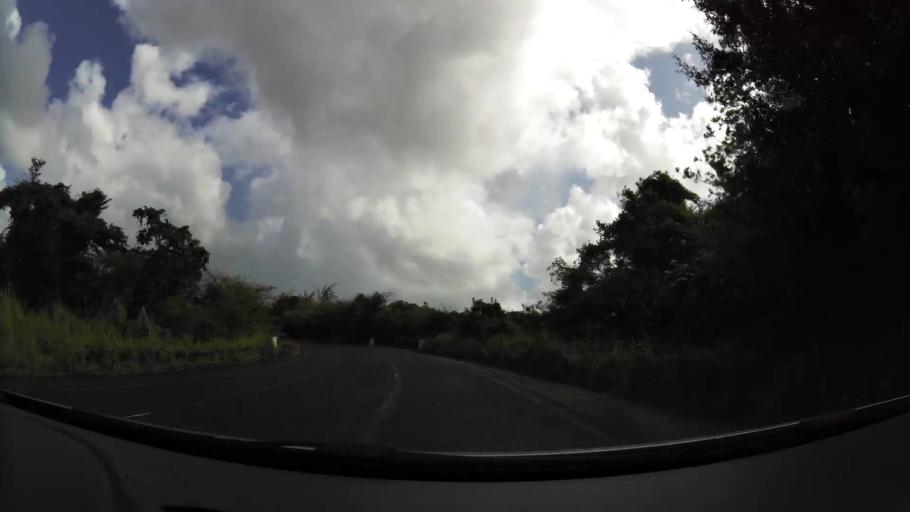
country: MQ
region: Martinique
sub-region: Martinique
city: Sainte-Luce
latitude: 14.4946
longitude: -60.9868
